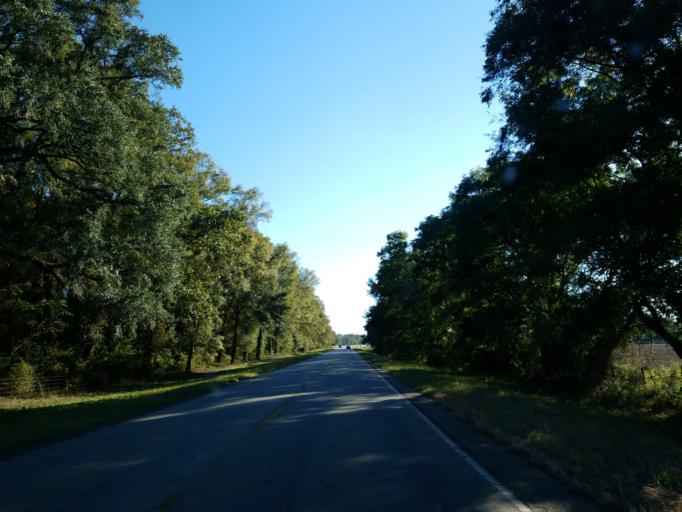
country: US
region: Georgia
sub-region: Lee County
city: Leesburg
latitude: 31.7553
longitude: -84.1537
